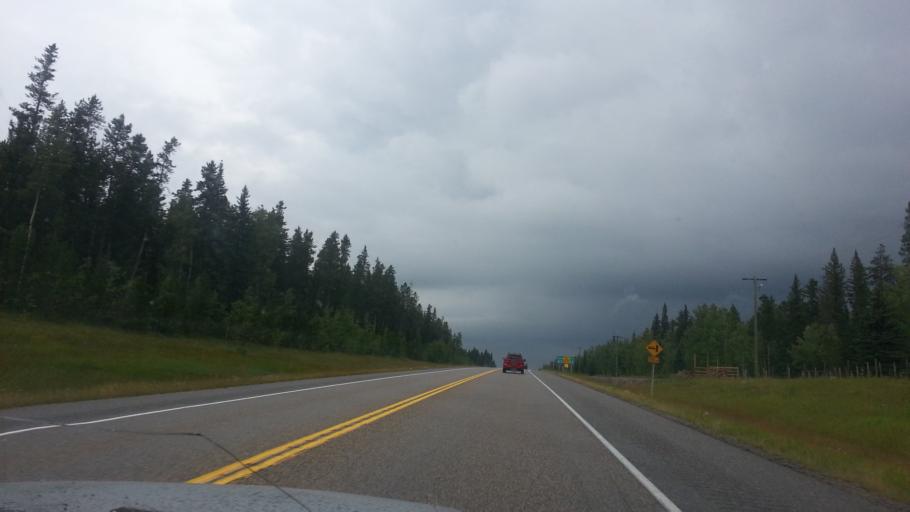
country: CA
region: Alberta
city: Cochrane
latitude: 50.9318
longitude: -114.5601
